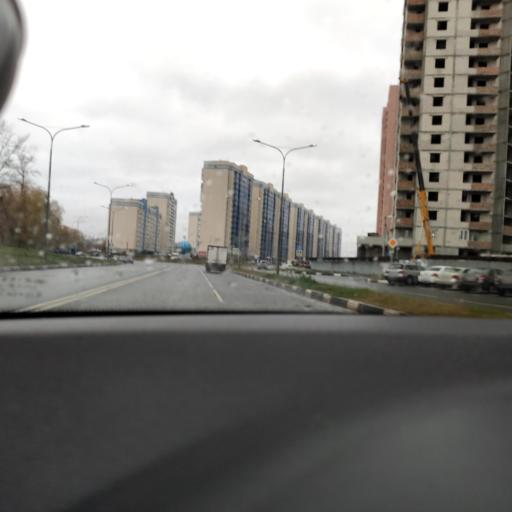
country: RU
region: Samara
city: Rozhdestveno
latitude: 53.1472
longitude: 50.0751
